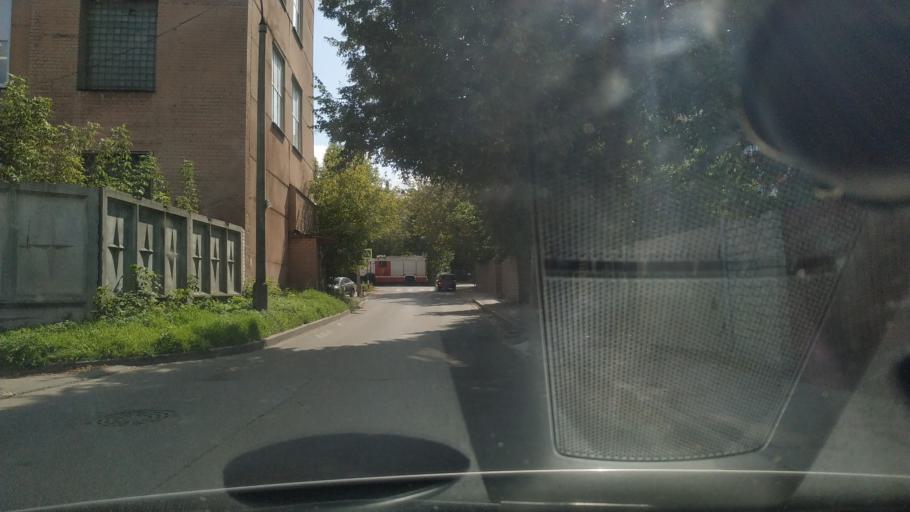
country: RU
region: Rjazan
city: Ryazan'
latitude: 54.6153
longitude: 39.7102
